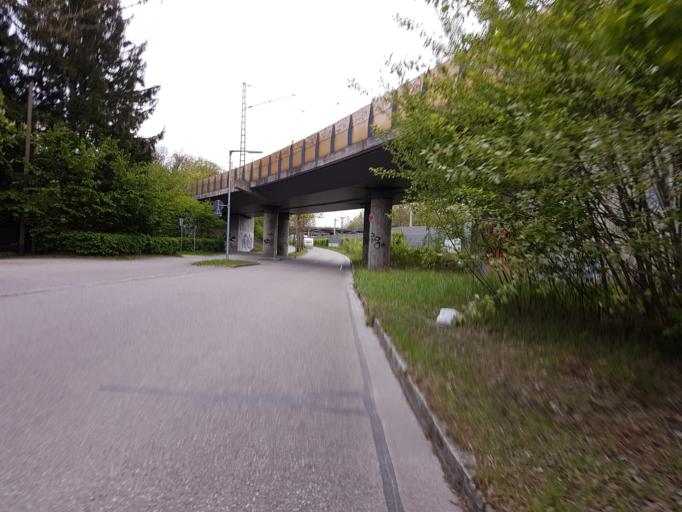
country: DE
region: Bavaria
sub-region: Upper Bavaria
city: Karlsfeld
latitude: 48.2073
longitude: 11.4618
